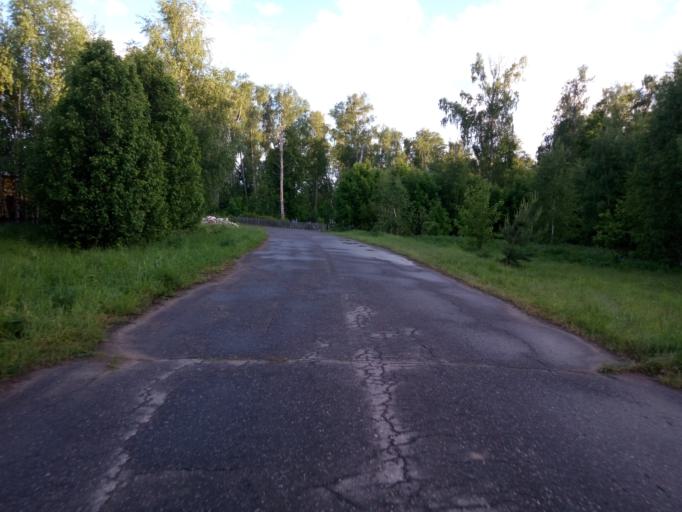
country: RU
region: Nizjnij Novgorod
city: Voskresenskoye
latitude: 56.7747
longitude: 45.5397
